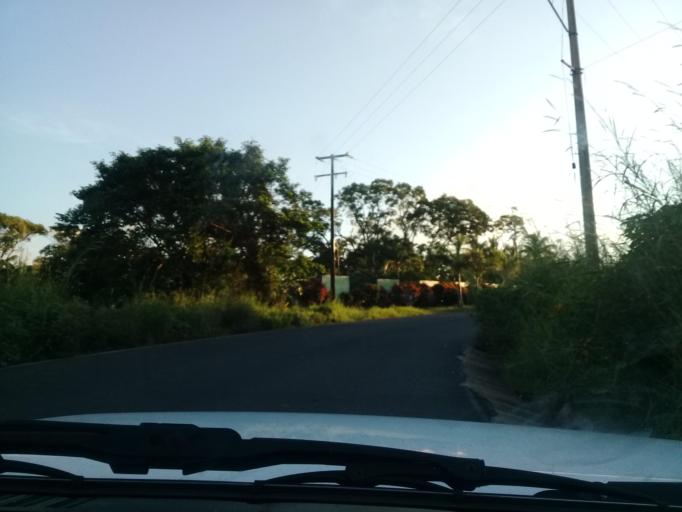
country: MX
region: Veracruz
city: Catemaco
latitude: 18.4255
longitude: -95.0951
